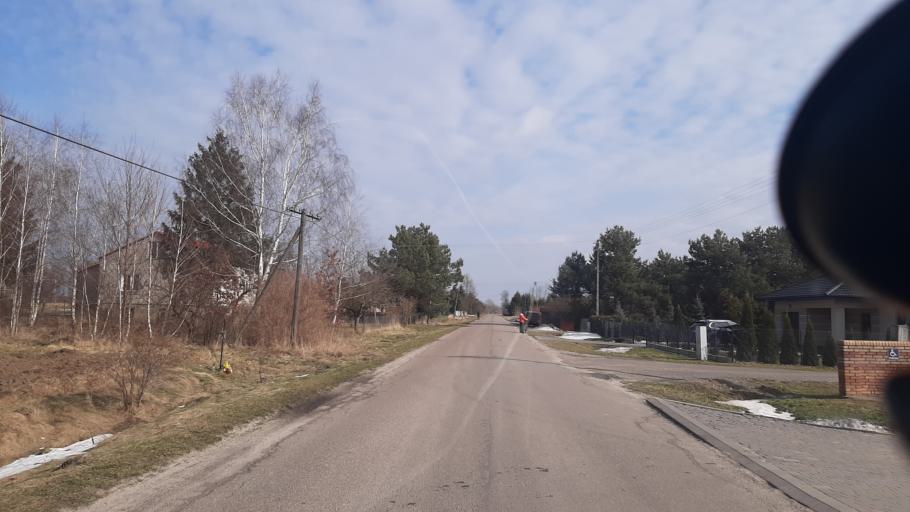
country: PL
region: Lublin Voivodeship
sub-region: Powiat lubartowski
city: Uscimow Stary
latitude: 51.4698
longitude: 22.9638
